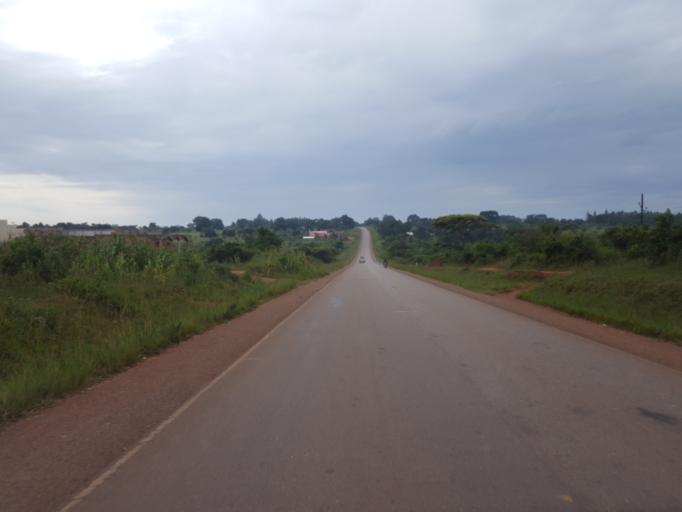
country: UG
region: Central Region
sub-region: Kyankwanzi District
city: Kyankwanzi
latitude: 1.1195
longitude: 31.6020
